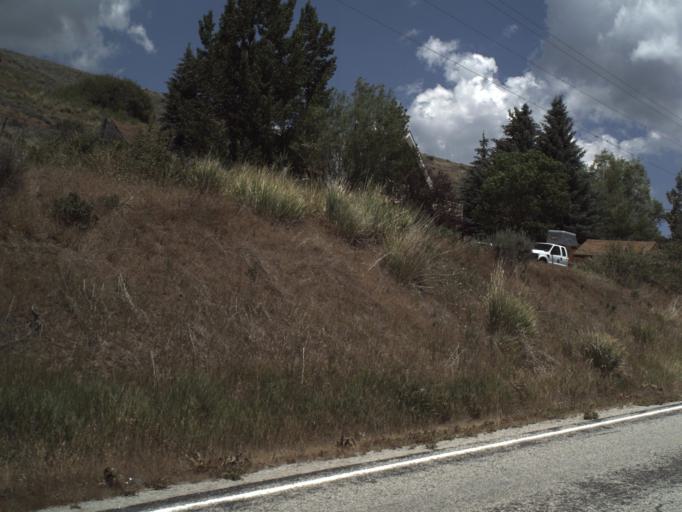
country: US
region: Utah
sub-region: Weber County
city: Wolf Creek
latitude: 41.2924
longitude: -111.6341
